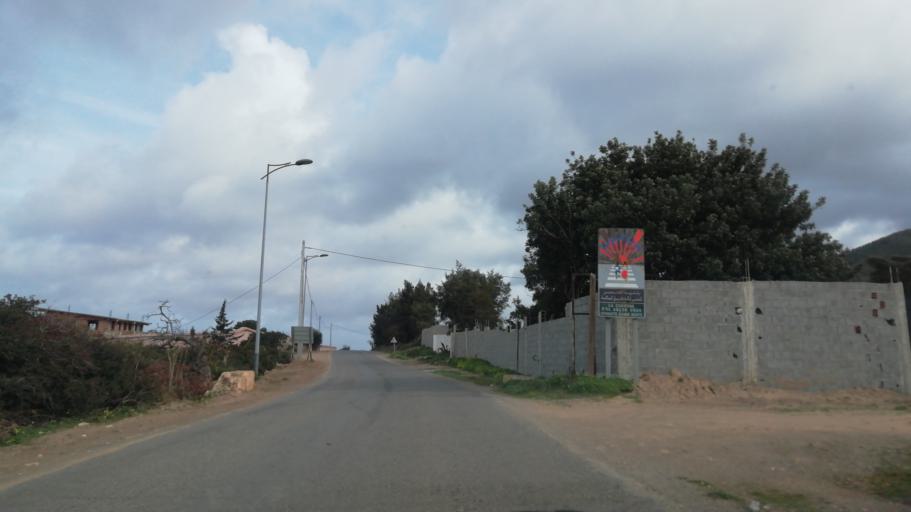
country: DZ
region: Oran
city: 'Ain el Turk
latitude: 35.6968
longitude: -0.8528
